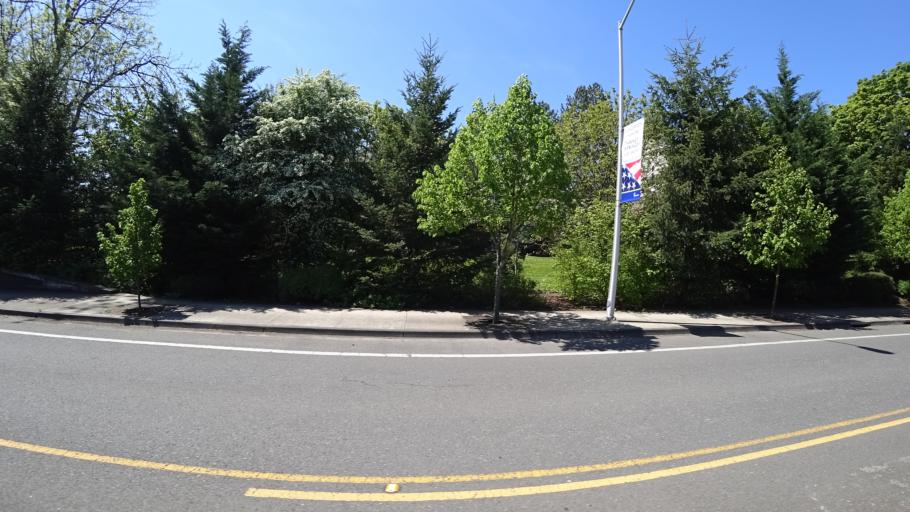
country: US
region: Oregon
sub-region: Washington County
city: King City
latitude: 45.4368
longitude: -122.8259
